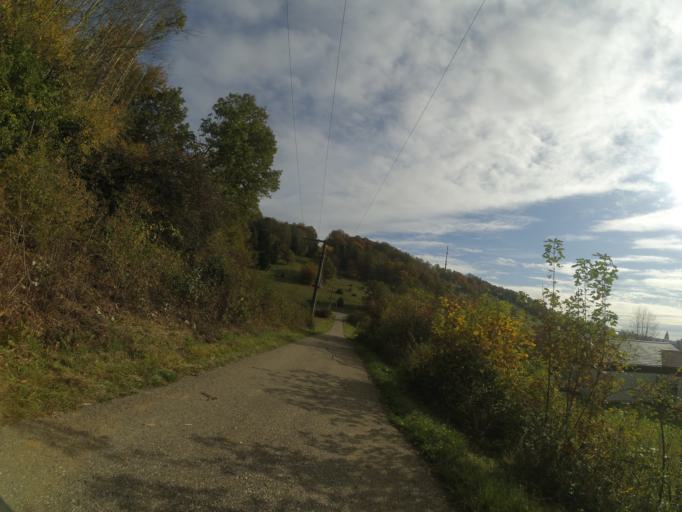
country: DE
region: Baden-Wuerttemberg
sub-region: Tuebingen Region
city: Lonsee
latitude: 48.5501
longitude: 9.9095
